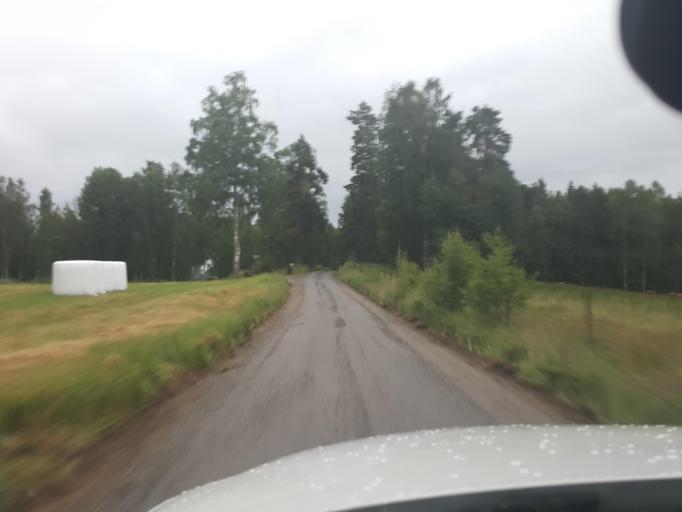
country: SE
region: Gaevleborg
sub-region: Bollnas Kommun
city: Kilafors
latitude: 61.2553
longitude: 16.6542
